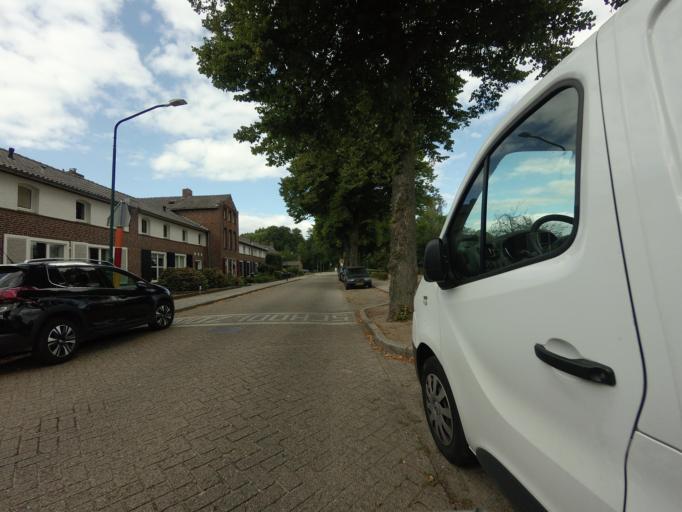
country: NL
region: North Brabant
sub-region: Gemeente Grave
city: Grave
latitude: 51.7584
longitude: 5.7315
